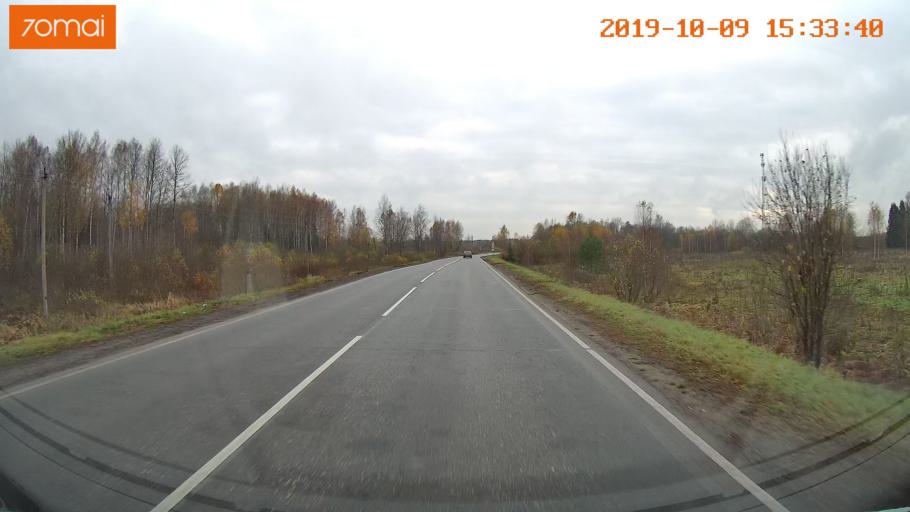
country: RU
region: Kostroma
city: Oktyabr'skiy
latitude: 57.9487
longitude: 41.2591
